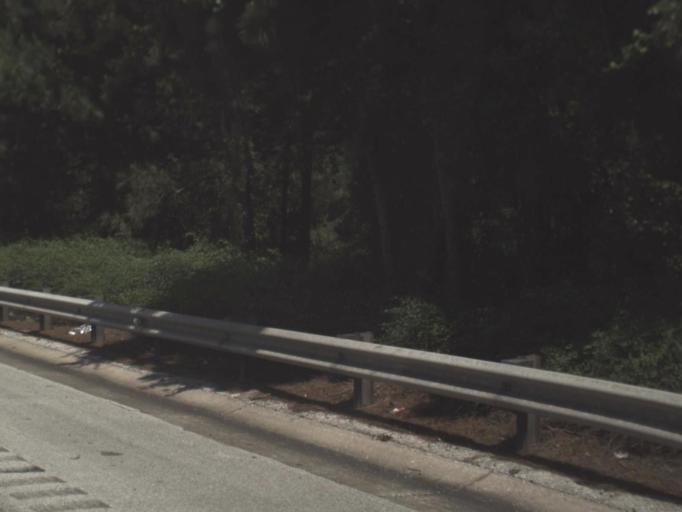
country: US
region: Florida
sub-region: Duval County
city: Baldwin
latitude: 30.2894
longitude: -81.9781
